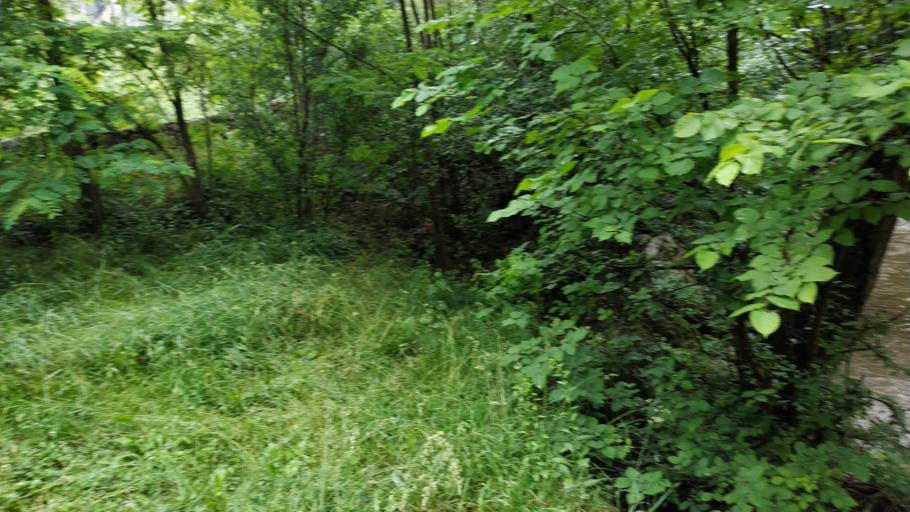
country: RS
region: Central Serbia
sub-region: Zajecarski Okrug
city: Soko Banja
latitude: 43.6363
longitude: 21.8880
